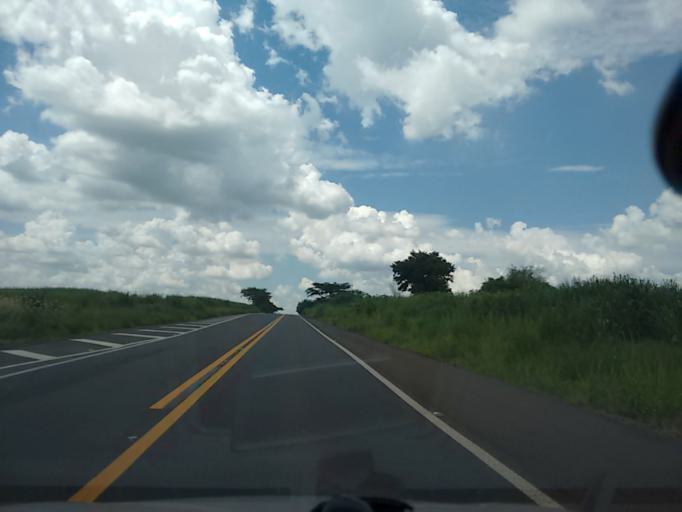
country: BR
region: Sao Paulo
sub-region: Osvaldo Cruz
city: Osvaldo Cruz
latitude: -21.8973
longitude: -50.8791
